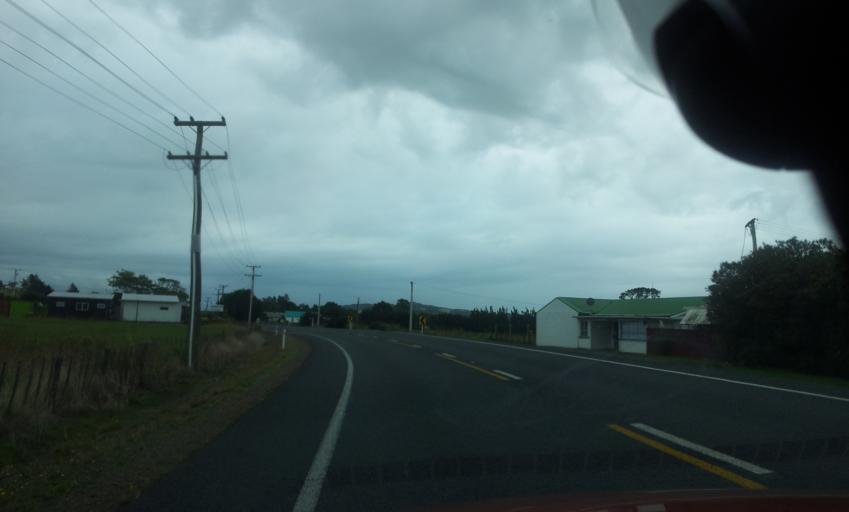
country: NZ
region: Northland
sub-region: Whangarei
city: Ruakaka
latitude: -35.8999
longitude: 174.4433
